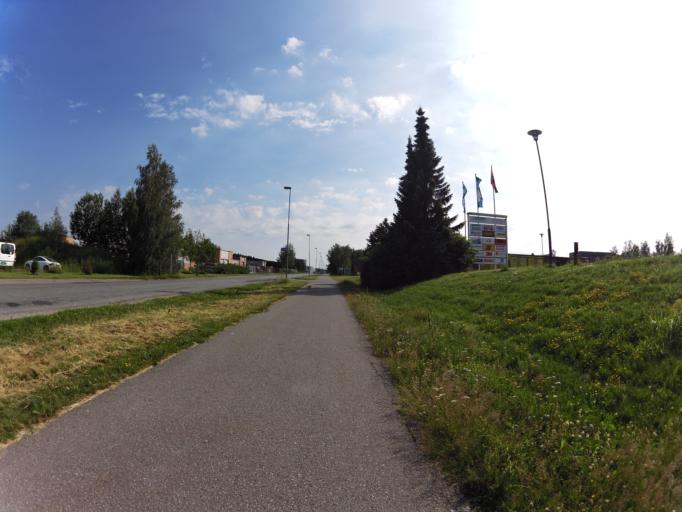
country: NO
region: Ostfold
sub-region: Fredrikstad
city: Fredrikstad
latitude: 59.2385
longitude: 10.9902
